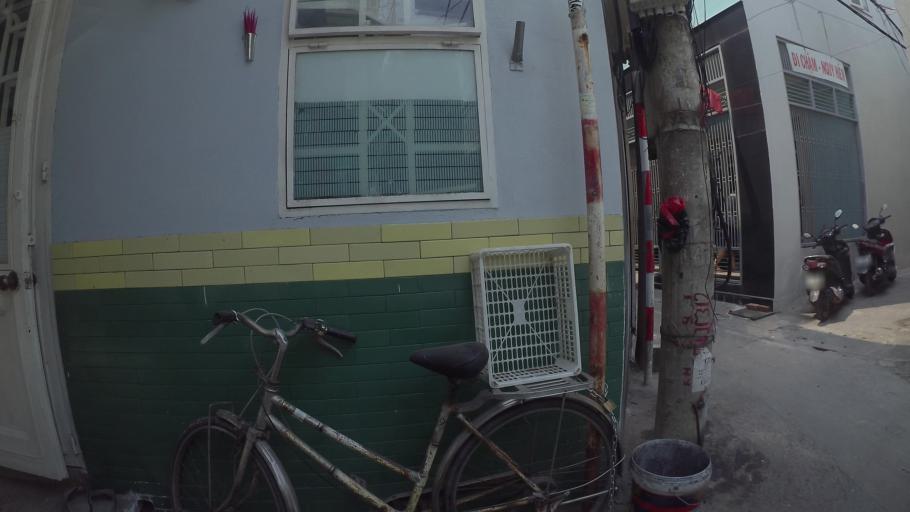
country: VN
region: Da Nang
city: Da Nang
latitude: 16.0789
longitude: 108.2163
